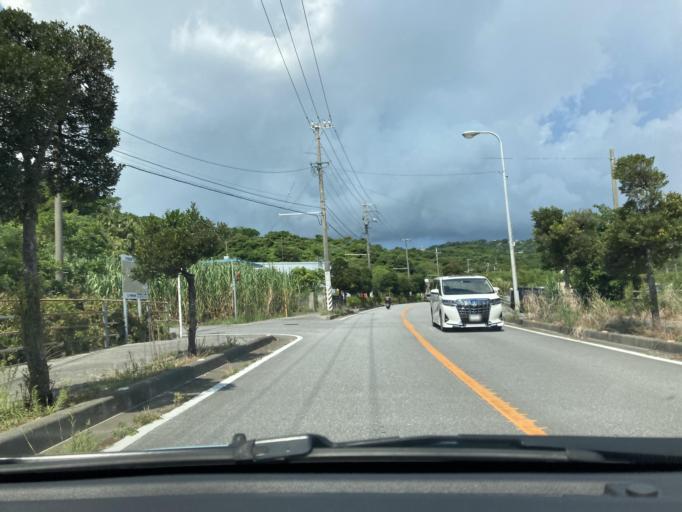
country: JP
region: Okinawa
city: Tomigusuku
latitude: 26.1731
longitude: 127.7691
